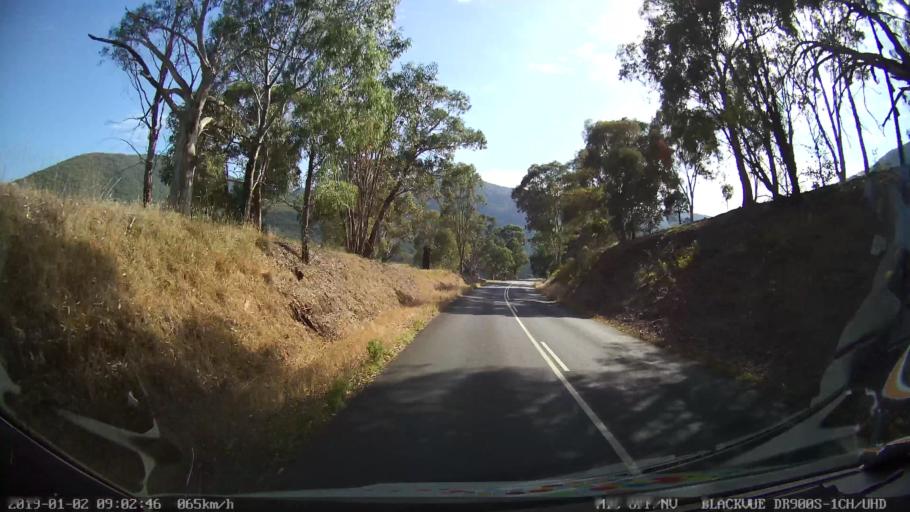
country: AU
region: New South Wales
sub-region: Tumut Shire
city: Tumut
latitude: -35.5706
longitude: 148.3155
